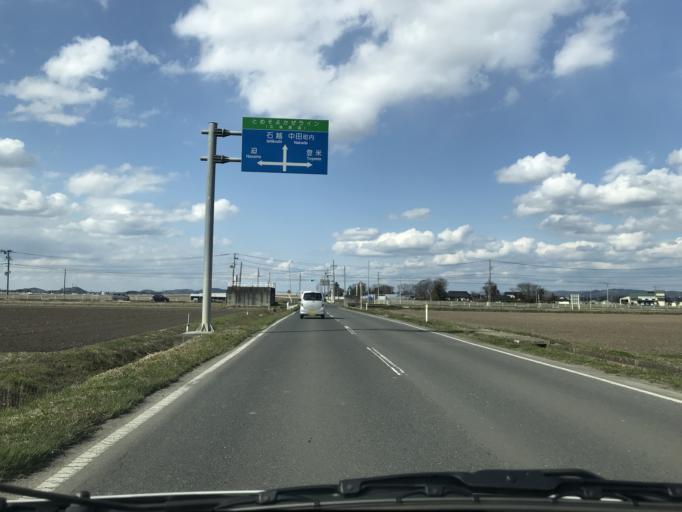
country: JP
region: Miyagi
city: Wakuya
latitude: 38.6769
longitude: 141.2319
